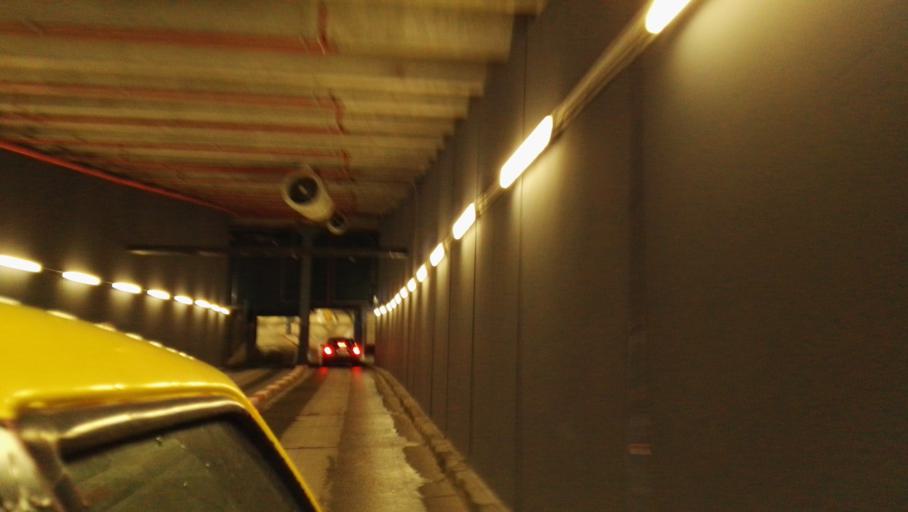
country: RO
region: Ilfov
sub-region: Comuna Fundeni-Dobroesti
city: Fundeni
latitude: 44.4420
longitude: 26.1528
